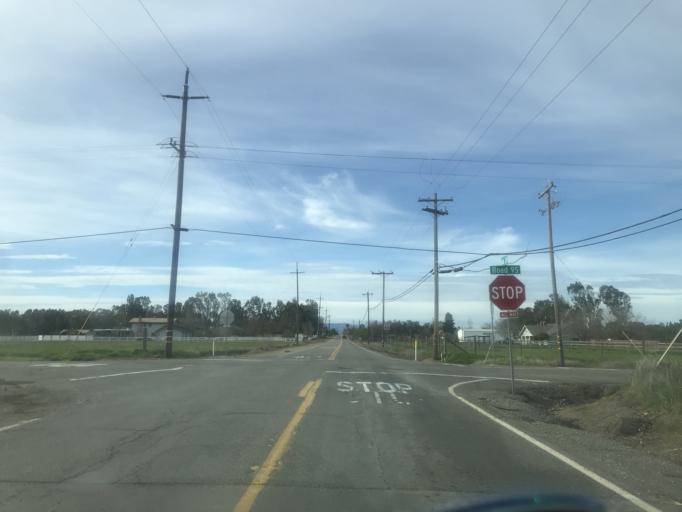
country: US
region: California
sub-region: Yolo County
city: Woodland
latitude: 38.6634
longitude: -121.8578
